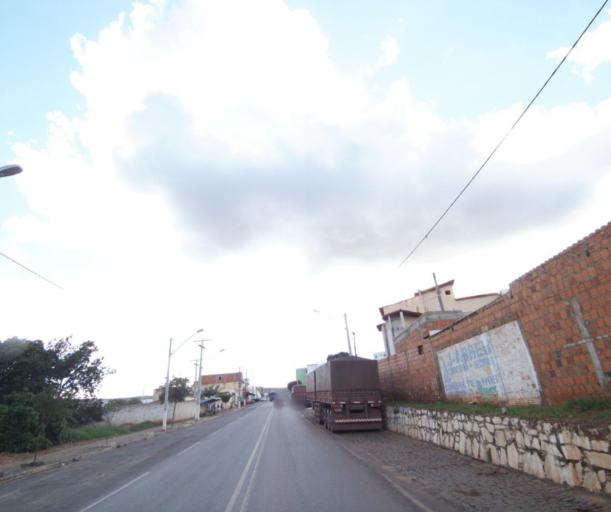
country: BR
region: Bahia
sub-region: Caetite
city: Caetite
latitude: -14.0652
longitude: -42.4792
